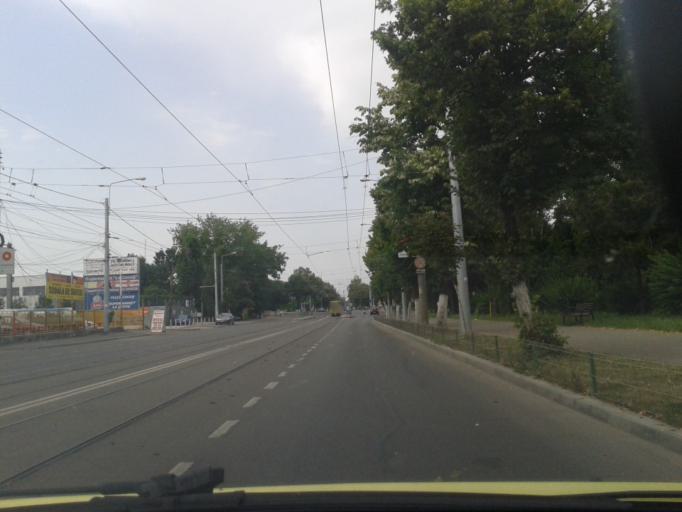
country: RO
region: Prahova
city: Ploiesti
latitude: 44.9413
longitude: 25.9914
